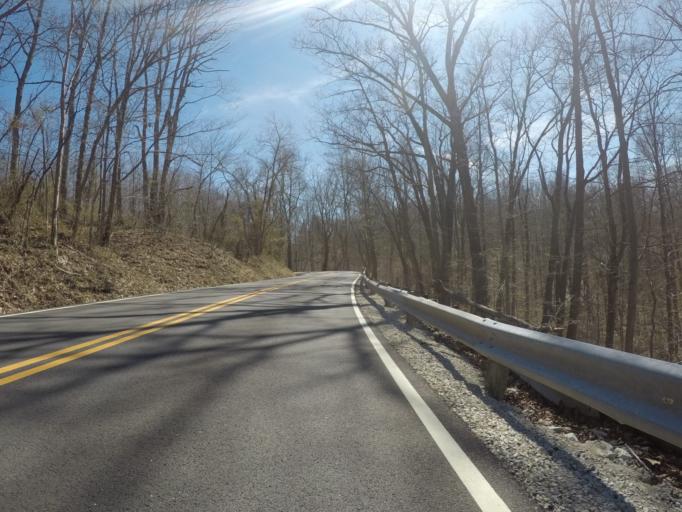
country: US
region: Ohio
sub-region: Lawrence County
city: South Point
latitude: 38.4593
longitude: -82.5540
